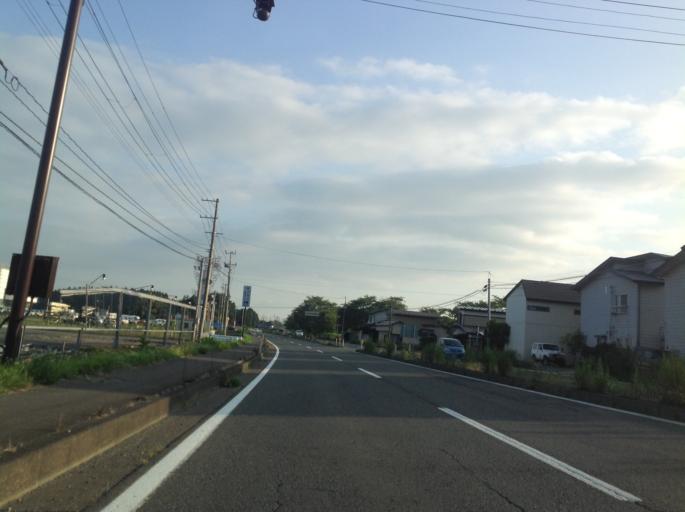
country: JP
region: Iwate
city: Hanamaki
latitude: 39.5340
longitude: 141.1659
